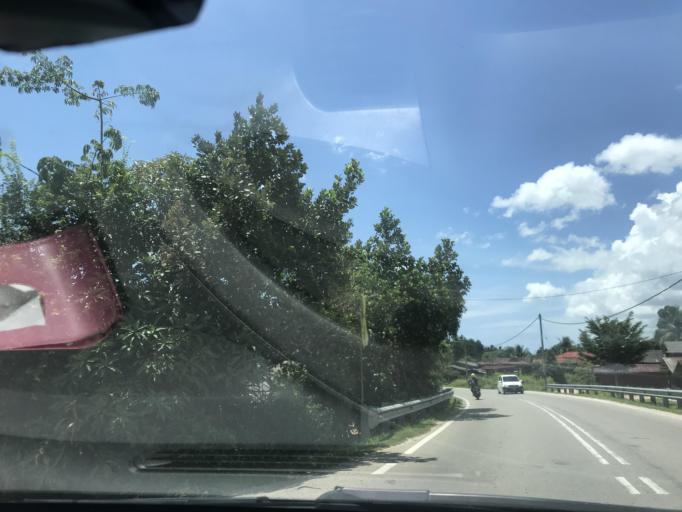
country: MY
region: Kelantan
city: Tumpat
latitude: 6.1931
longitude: 102.1471
